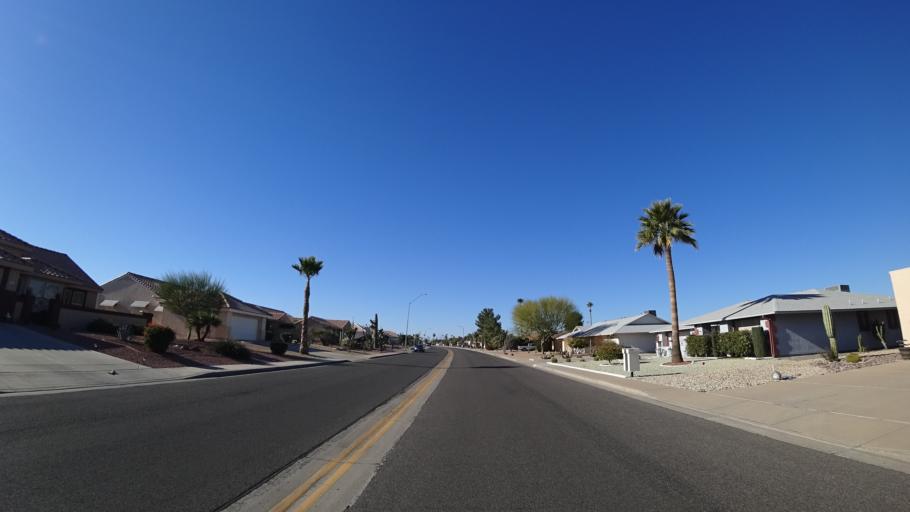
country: US
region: Arizona
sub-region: Maricopa County
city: Sun City West
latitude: 33.6688
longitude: -112.3416
